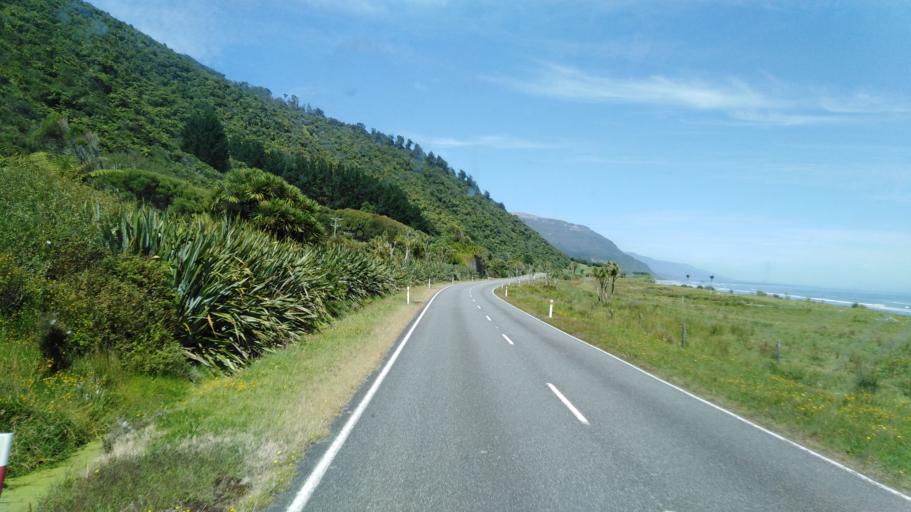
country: NZ
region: West Coast
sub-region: Buller District
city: Westport
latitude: -41.5835
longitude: 171.8964
